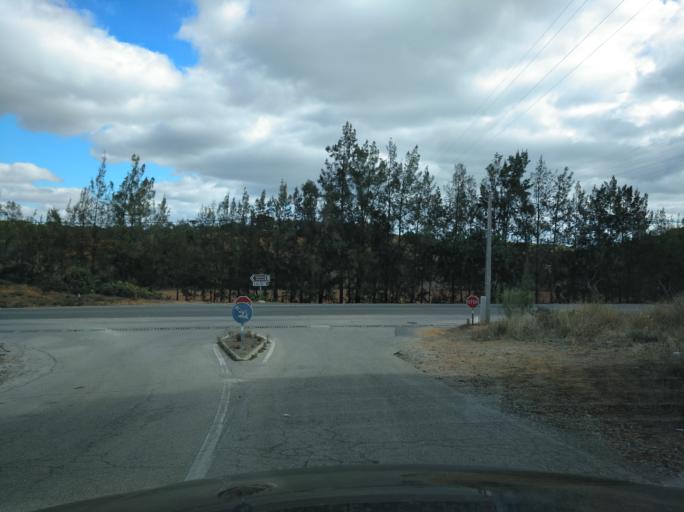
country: PT
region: Faro
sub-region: Vila Real de Santo Antonio
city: Monte Gordo
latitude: 37.1876
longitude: -7.4847
